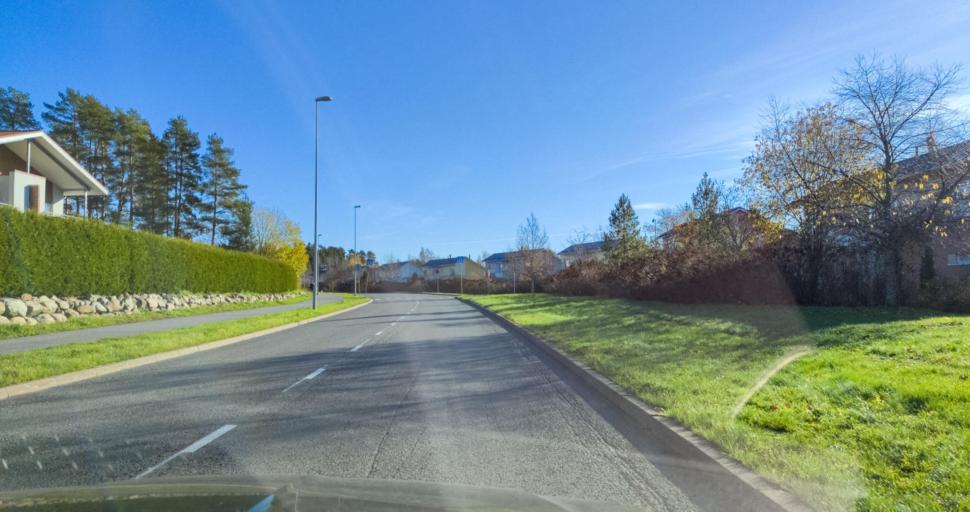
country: FI
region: Varsinais-Suomi
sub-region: Turku
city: Turku
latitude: 60.4095
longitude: 22.2170
